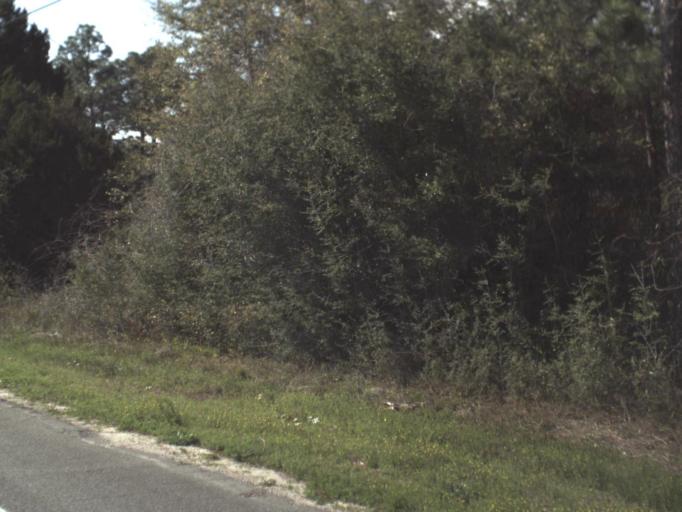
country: US
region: Florida
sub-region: Wakulla County
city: Crawfordville
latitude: 30.0759
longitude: -84.4287
